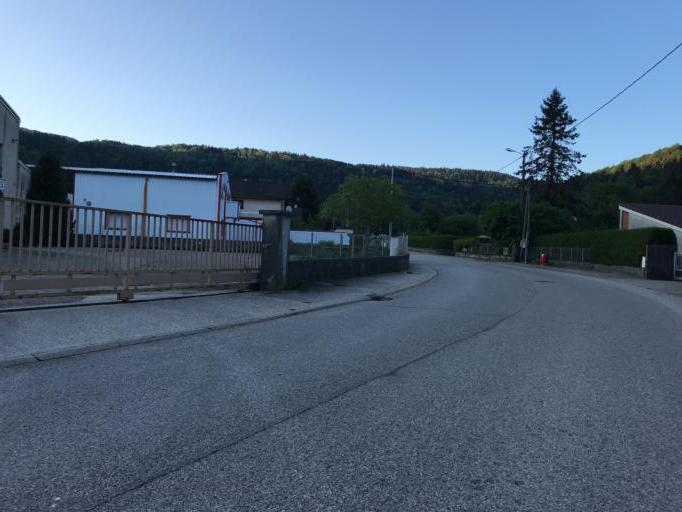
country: FR
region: Rhone-Alpes
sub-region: Departement de l'Ain
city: Oyonnax
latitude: 46.2406
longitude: 5.6670
